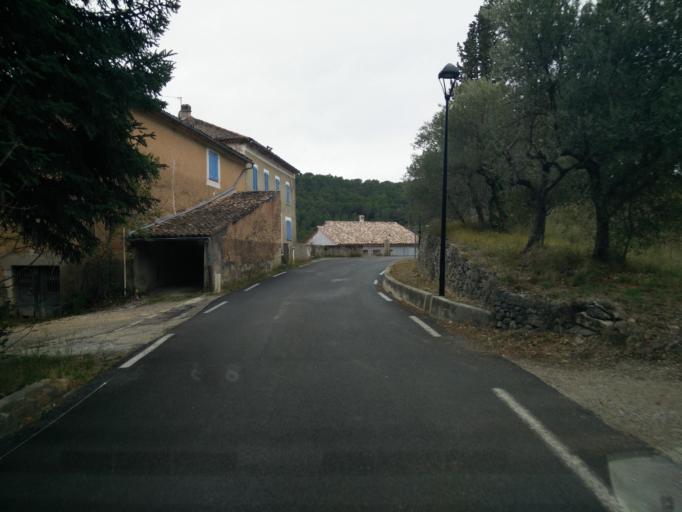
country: FR
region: Provence-Alpes-Cote d'Azur
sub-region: Departement du Var
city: Cotignac
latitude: 43.5254
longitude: 6.1541
